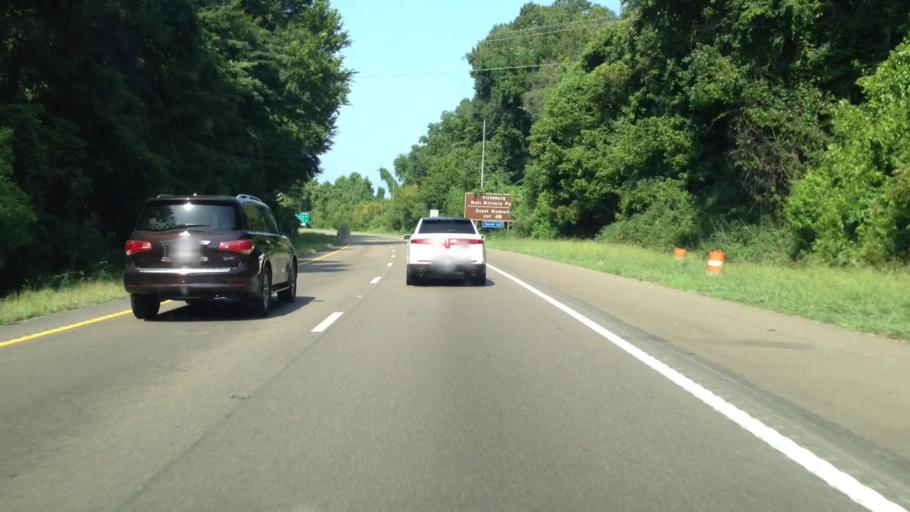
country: US
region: Mississippi
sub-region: Warren County
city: Beechwood
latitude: 32.3476
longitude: -90.8360
